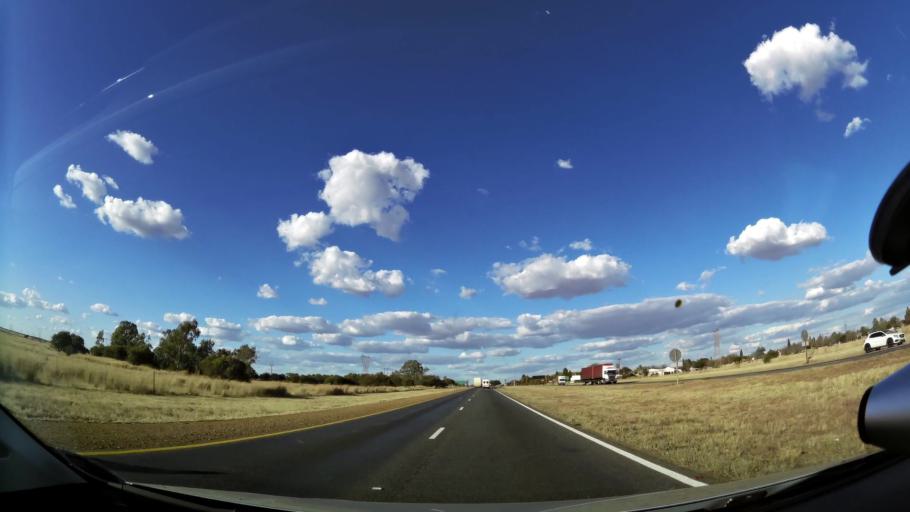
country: ZA
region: North-West
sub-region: Dr Kenneth Kaunda District Municipality
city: Stilfontein
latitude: -26.8431
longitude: 26.7394
